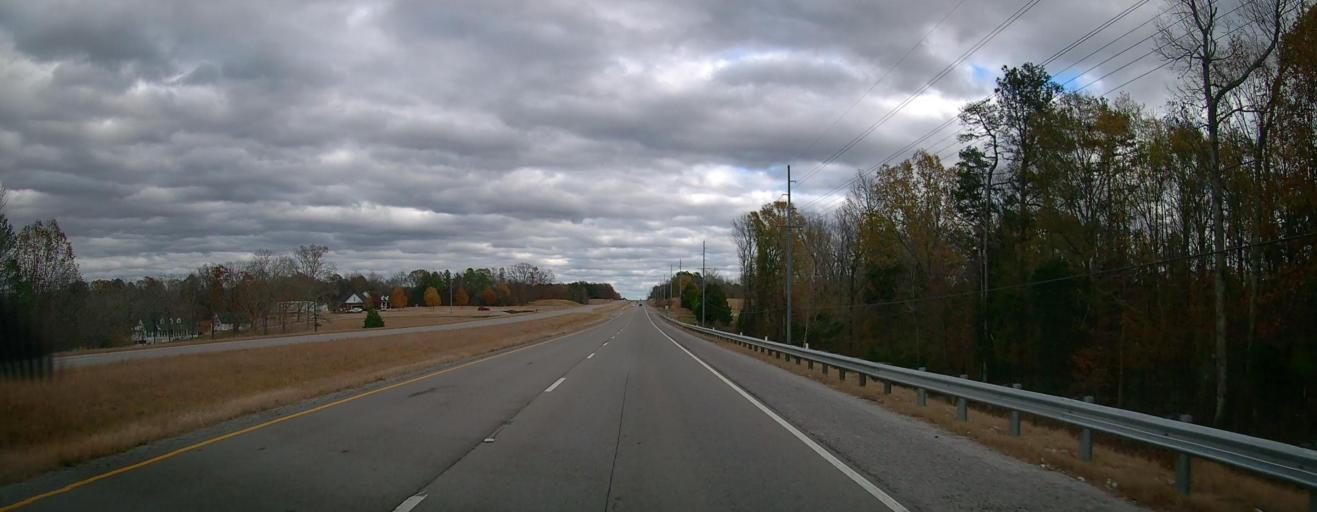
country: US
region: Alabama
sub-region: Lawrence County
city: Town Creek
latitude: 34.5728
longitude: -87.3937
